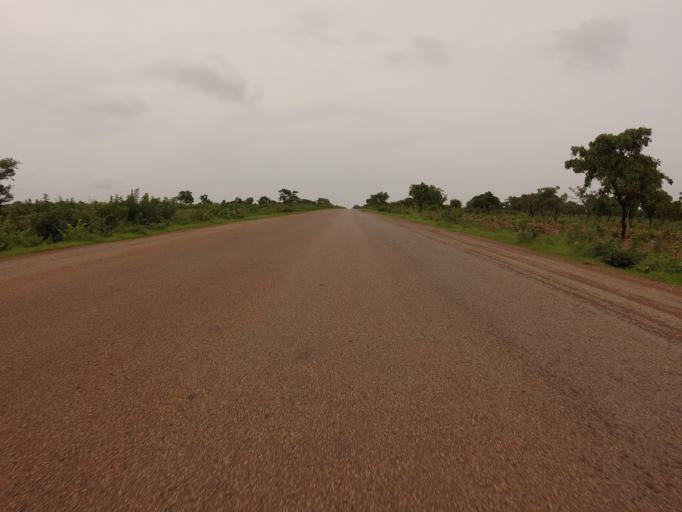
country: GH
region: Northern
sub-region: Yendi
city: Yendi
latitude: 9.3552
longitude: 0.0002
